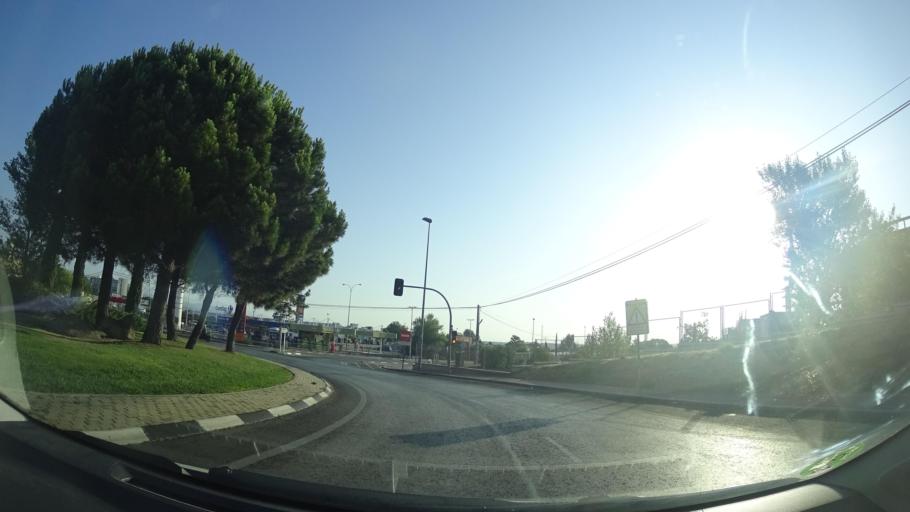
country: ES
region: Madrid
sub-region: Provincia de Madrid
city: Las Rozas de Madrid
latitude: 40.5208
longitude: -3.8854
